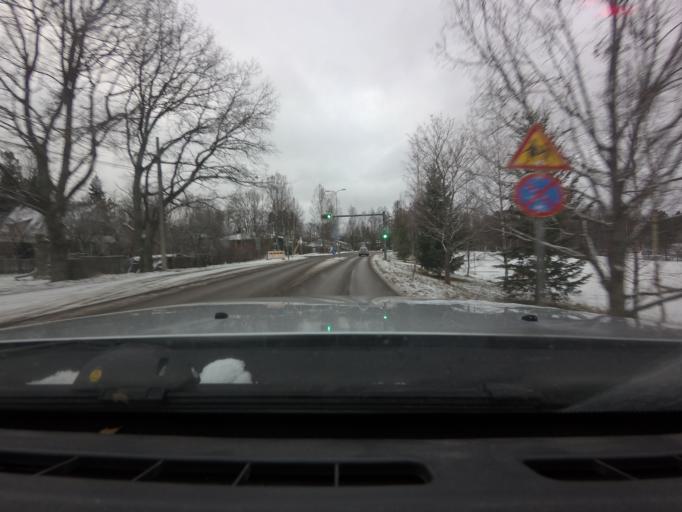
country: FI
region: Uusimaa
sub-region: Helsinki
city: Kauniainen
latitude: 60.2445
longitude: 24.7495
